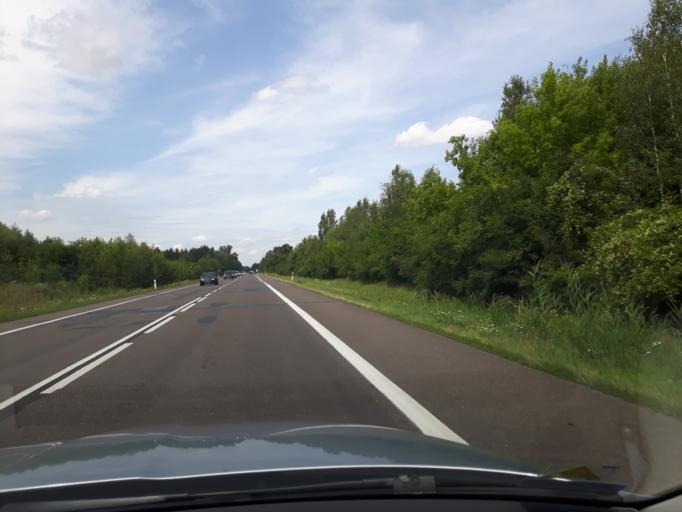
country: PL
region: Masovian Voivodeship
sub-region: Powiat ciechanowski
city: Glinojeck
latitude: 52.8105
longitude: 20.2691
